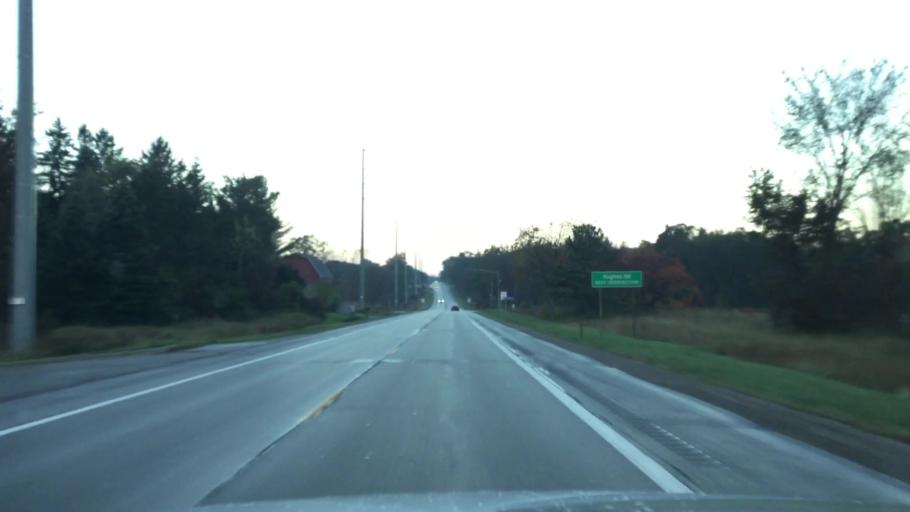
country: US
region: Michigan
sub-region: Livingston County
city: Howell
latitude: 42.6303
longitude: -83.8532
